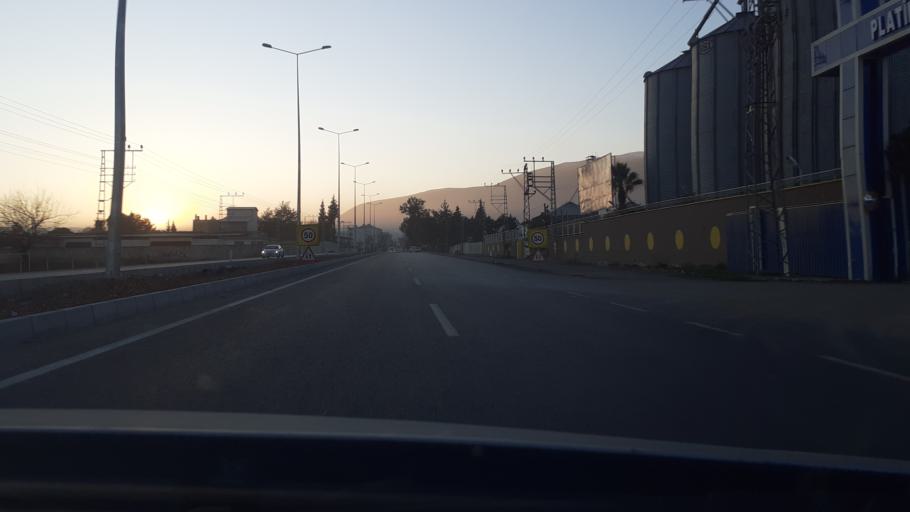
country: TR
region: Hatay
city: Kirikhan
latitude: 36.5009
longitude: 36.3798
